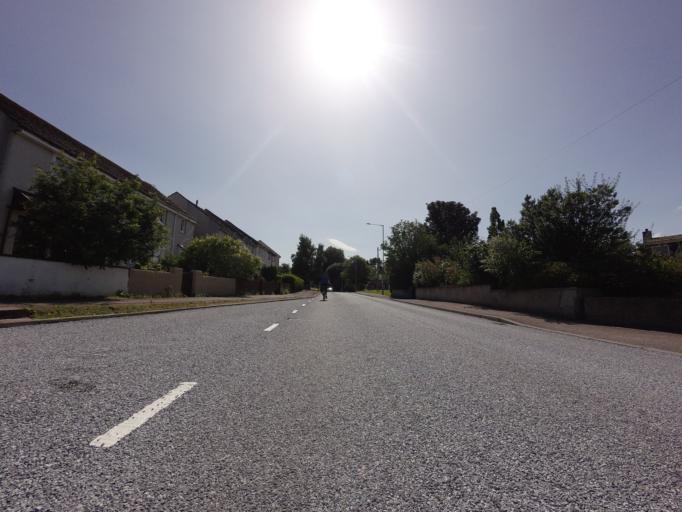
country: GB
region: Scotland
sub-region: Highland
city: Inverness
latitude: 57.4802
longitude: -4.1521
